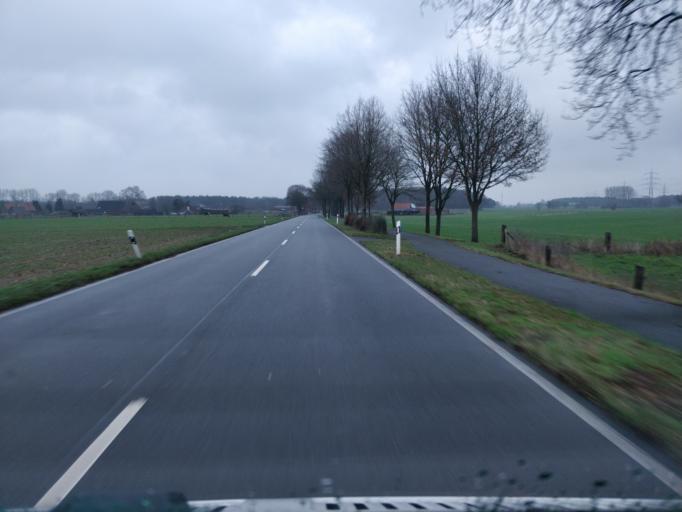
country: DE
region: North Rhine-Westphalia
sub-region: Regierungsbezirk Dusseldorf
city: Mehrhoog
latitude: 51.7588
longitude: 6.5189
